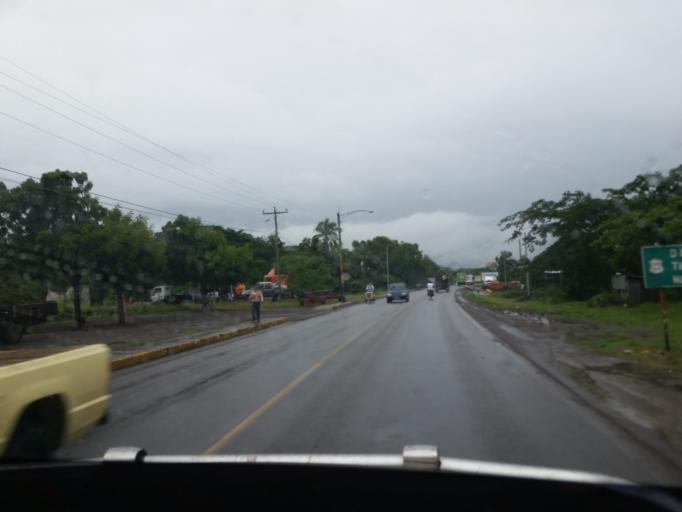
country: NI
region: Matagalpa
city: Ciudad Dario
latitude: 12.8475
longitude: -86.1007
